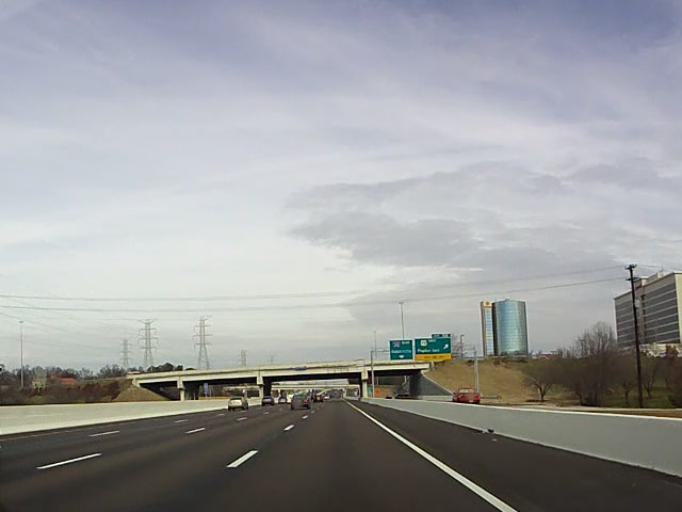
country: US
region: Tennessee
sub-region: Shelby County
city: Germantown
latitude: 35.1019
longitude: -89.8700
